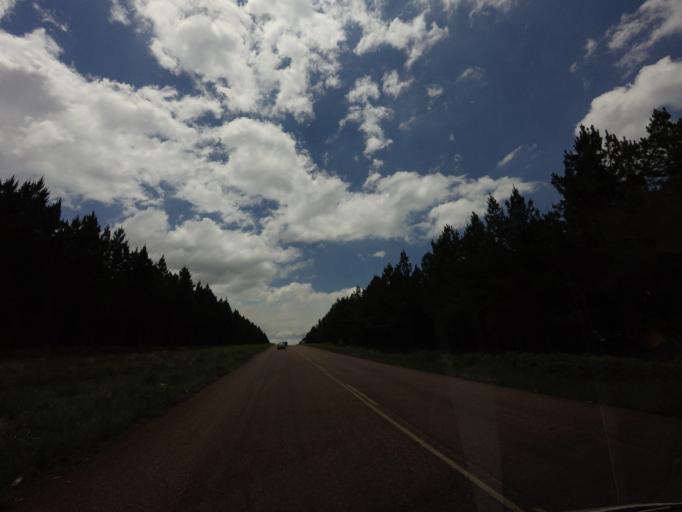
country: ZA
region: Mpumalanga
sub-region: Ehlanzeni District
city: Graksop
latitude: -25.0373
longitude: 30.8205
